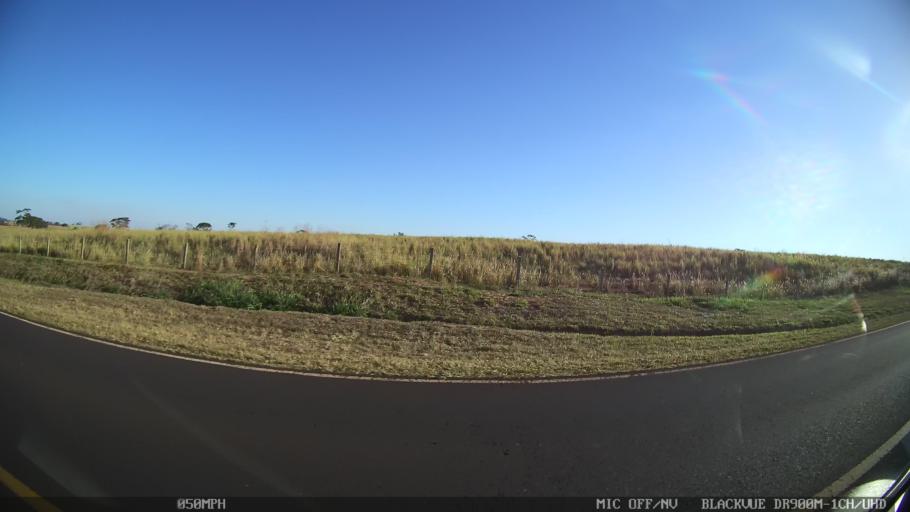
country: BR
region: Sao Paulo
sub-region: Guapiacu
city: Guapiacu
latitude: -20.7857
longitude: -49.2553
